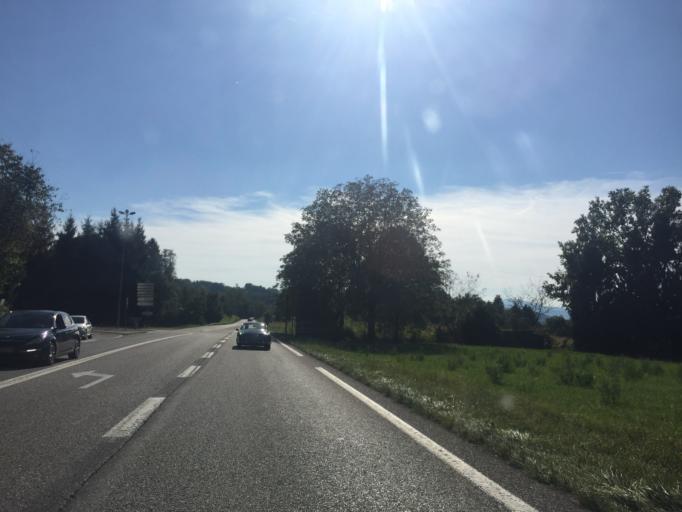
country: FR
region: Rhone-Alpes
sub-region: Departement de la Haute-Savoie
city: Viuz-la-Chiesaz
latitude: 45.8326
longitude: 6.0538
